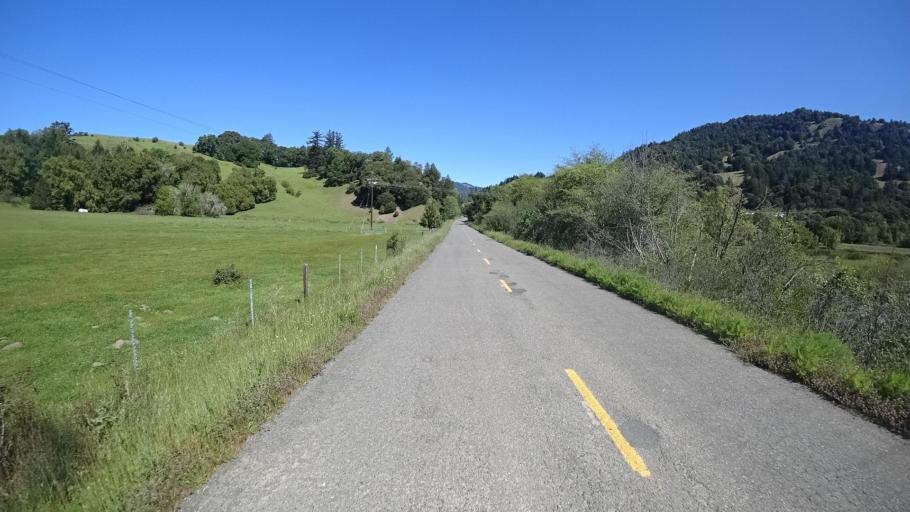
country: US
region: California
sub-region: Humboldt County
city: Rio Dell
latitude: 40.2388
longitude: -124.1215
